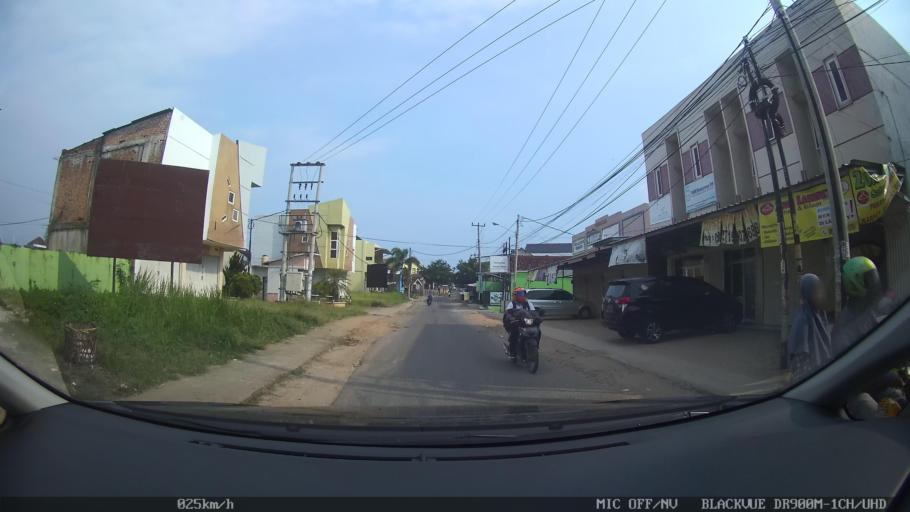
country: ID
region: Lampung
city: Kedaton
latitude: -5.3664
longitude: 105.2208
